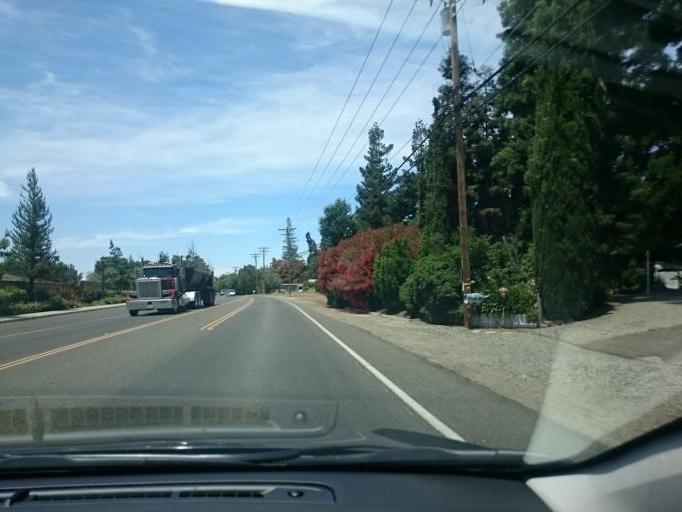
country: US
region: California
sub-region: Stanislaus County
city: Waterford
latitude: 37.6398
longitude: -120.7498
